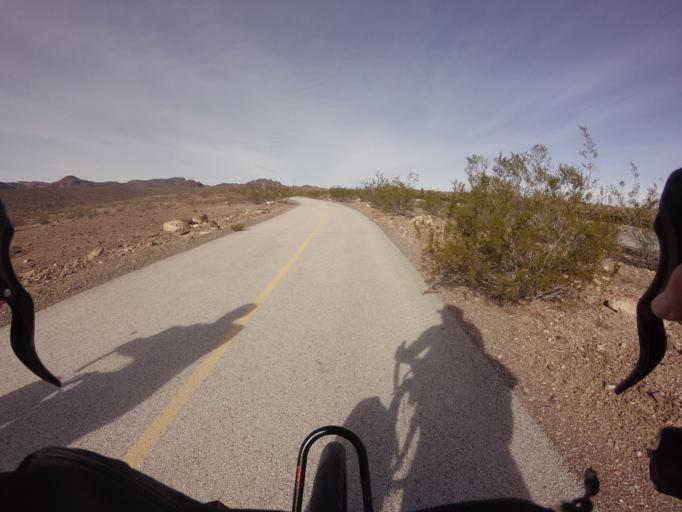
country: US
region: Nevada
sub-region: Clark County
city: Boulder City
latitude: 36.0764
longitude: -114.8142
